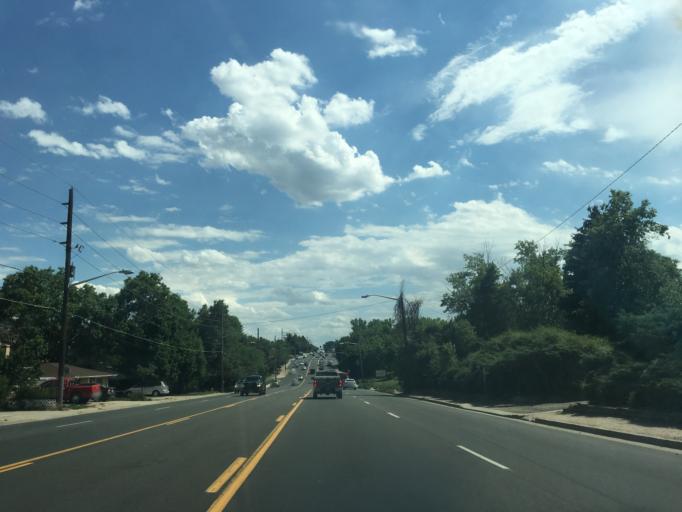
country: US
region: Colorado
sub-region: Jefferson County
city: Lakewood
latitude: 39.6854
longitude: -105.0533
